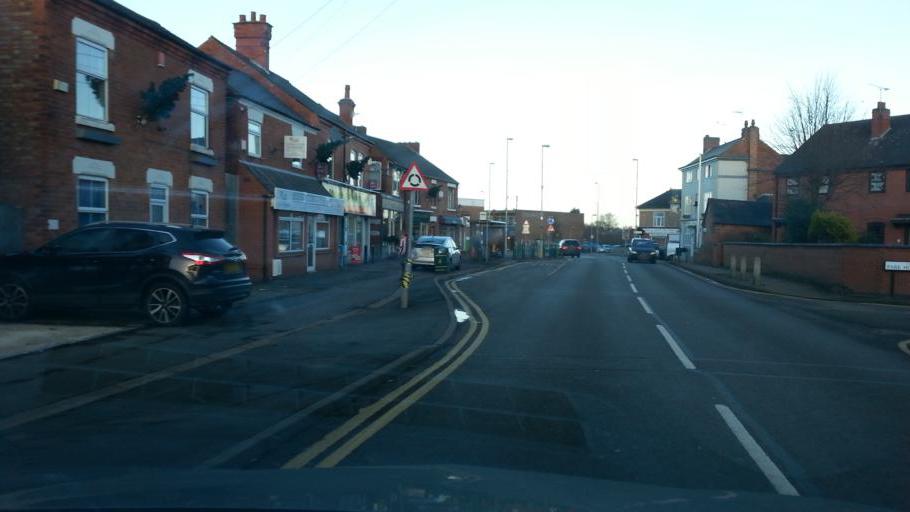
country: GB
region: England
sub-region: Leicestershire
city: Blaby
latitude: 52.5738
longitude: -1.1643
